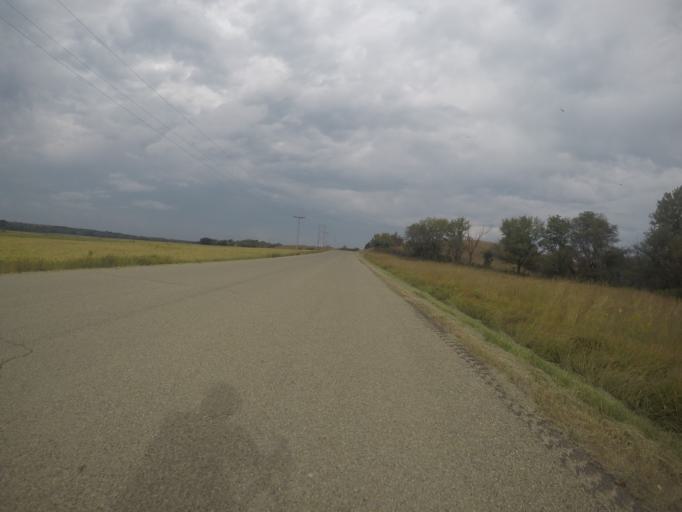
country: US
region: Kansas
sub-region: Riley County
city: Ogden
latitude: 38.9349
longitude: -96.5905
